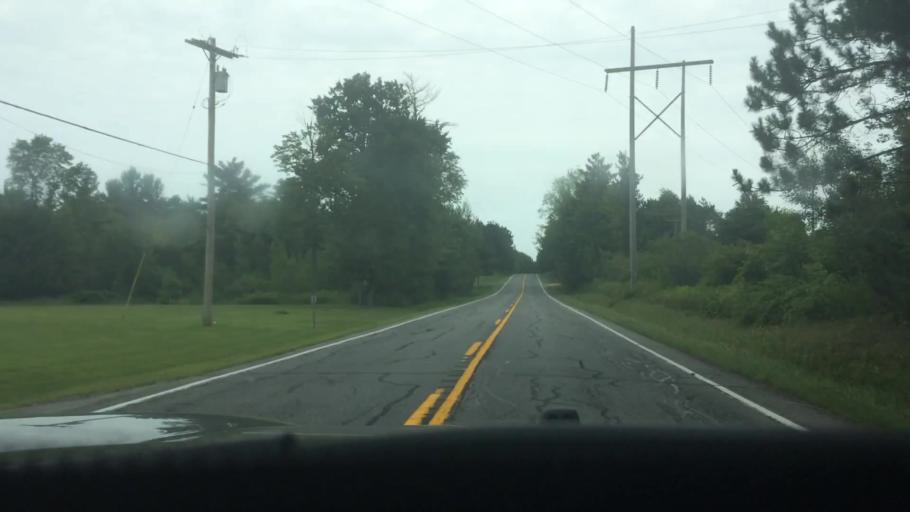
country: US
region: New York
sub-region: St. Lawrence County
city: Hannawa Falls
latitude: 44.6671
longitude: -74.7392
